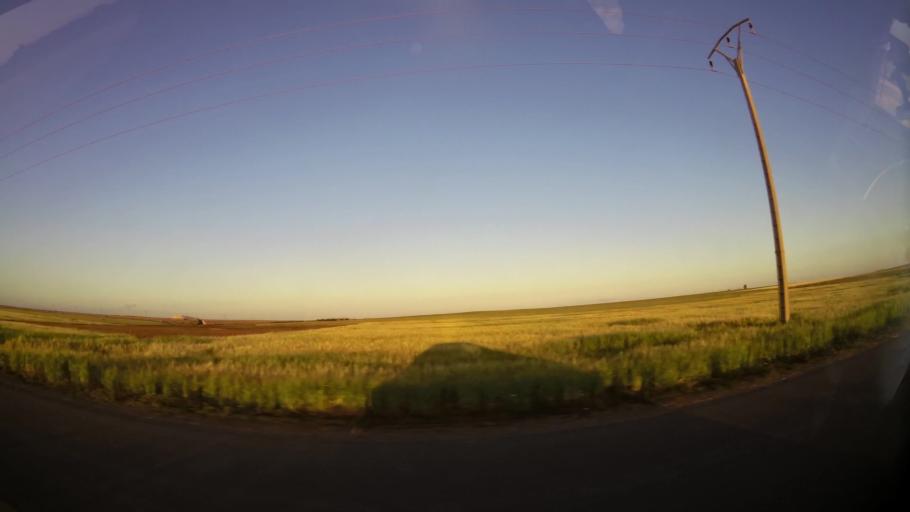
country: MA
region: Marrakech-Tensift-Al Haouz
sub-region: Kelaa-Des-Sraghna
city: Sidi Abdallah
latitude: 32.2342
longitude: -7.9289
